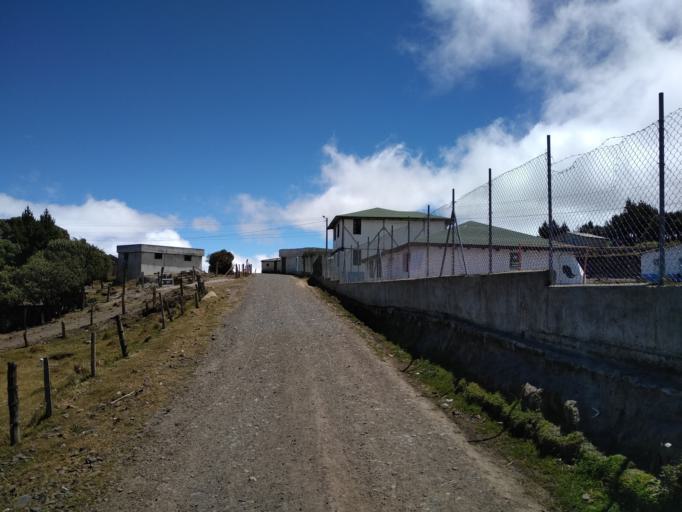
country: EC
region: Cotopaxi
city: Pujili
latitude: -0.9701
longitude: -78.9294
